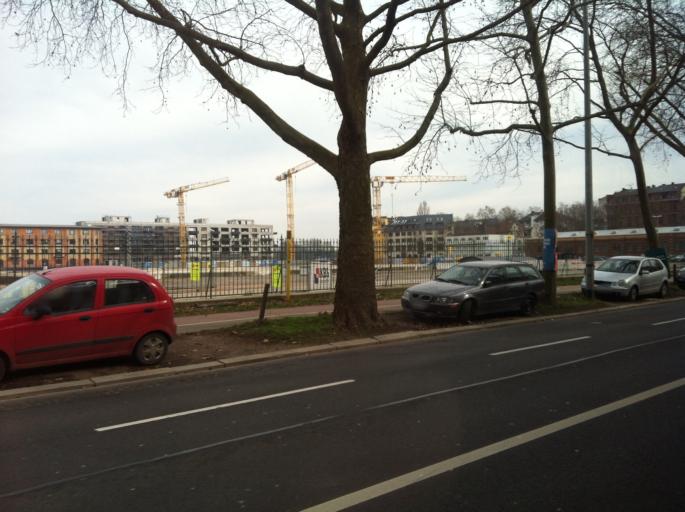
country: DE
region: Rheinland-Pfalz
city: Mainz
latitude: 50.0128
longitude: 8.2601
